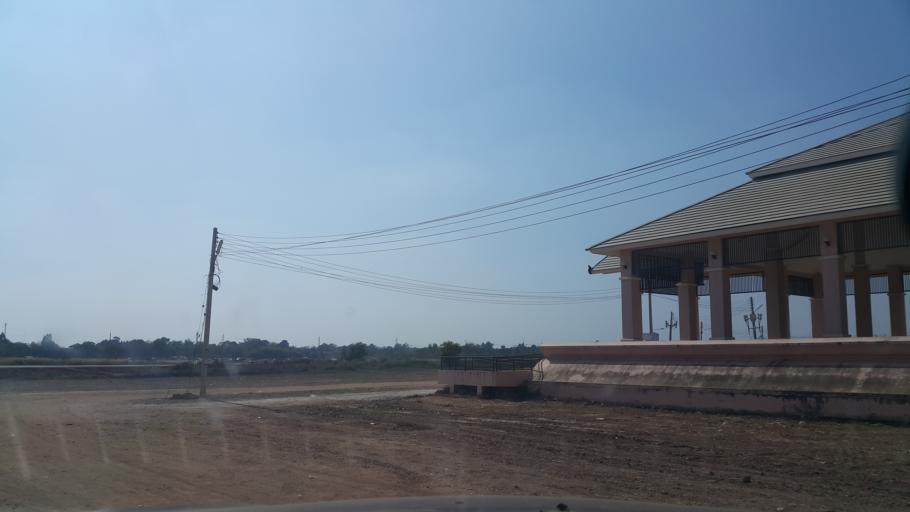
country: TH
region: Khon Kaen
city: Khon Kaen
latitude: 16.5099
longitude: 102.8716
